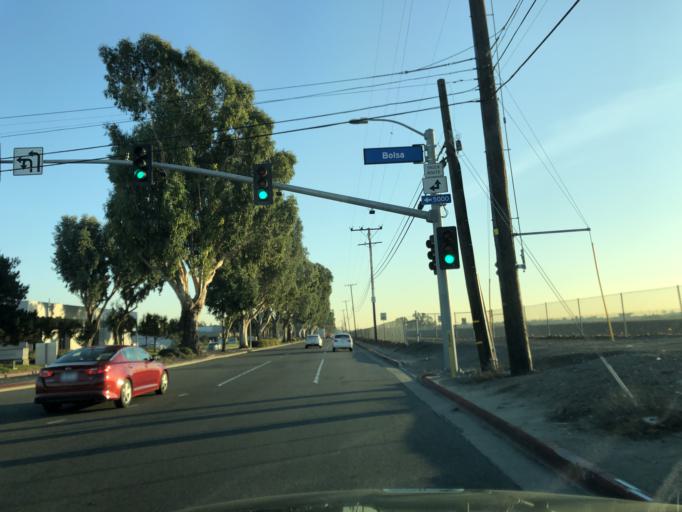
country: US
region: California
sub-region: Orange County
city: Westminster
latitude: 33.7445
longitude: -118.0419
